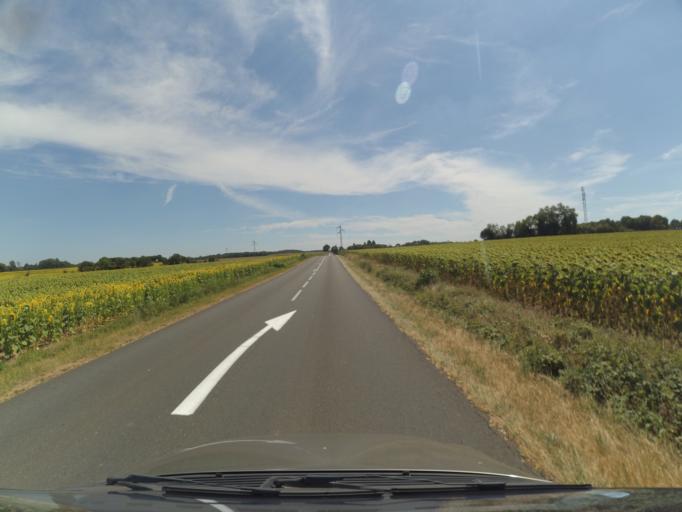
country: FR
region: Poitou-Charentes
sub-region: Departement de la Vienne
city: Usson-du-Poitou
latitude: 46.2940
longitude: 0.5075
